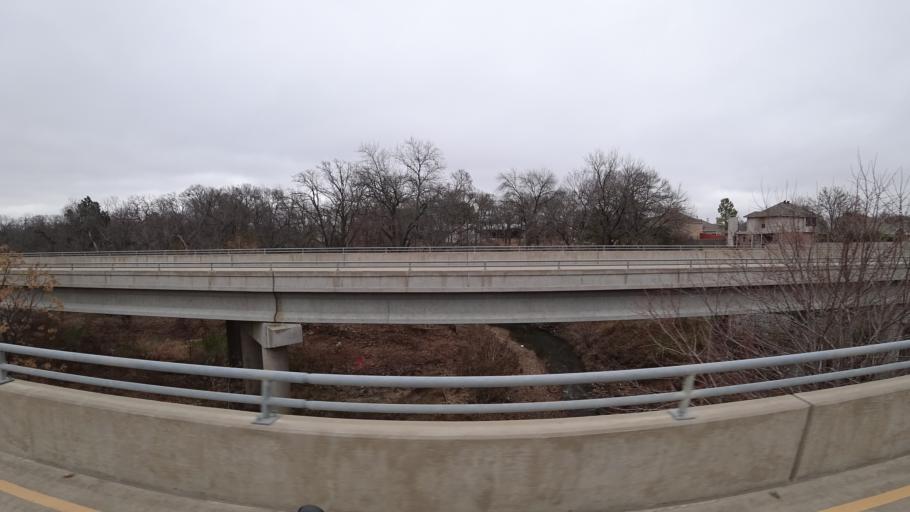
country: US
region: Texas
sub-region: Denton County
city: Lewisville
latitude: 33.0264
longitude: -97.0365
